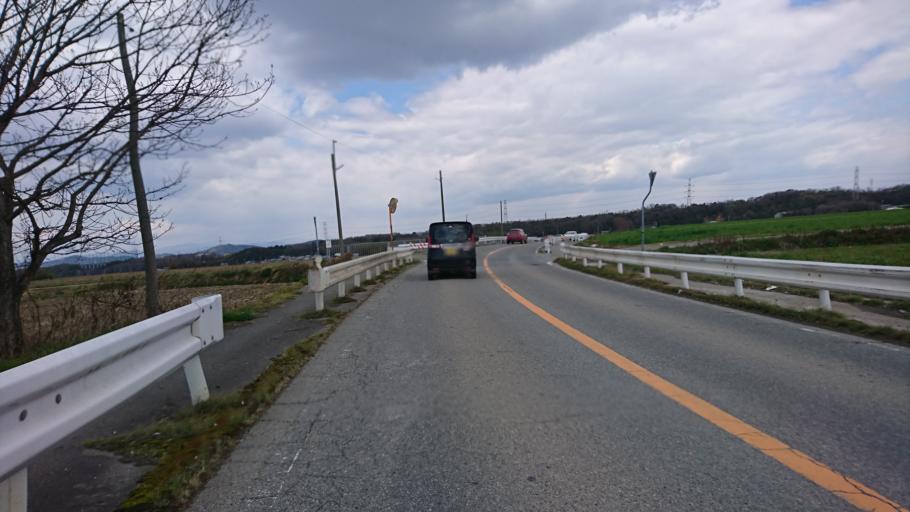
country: JP
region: Hyogo
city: Miki
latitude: 34.7617
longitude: 134.9500
